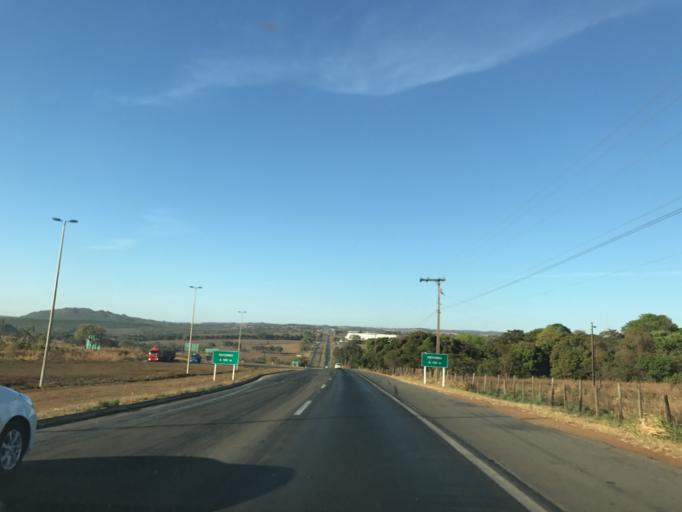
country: BR
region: Goias
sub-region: Aparecida De Goiania
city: Aparecida de Goiania
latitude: -16.8430
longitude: -49.2457
